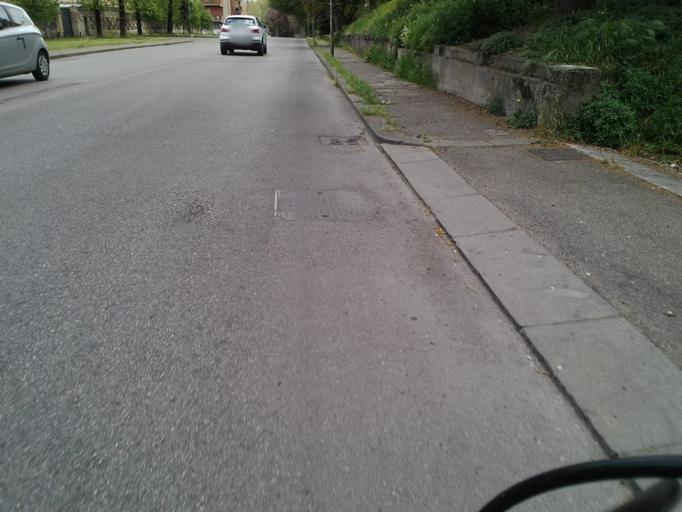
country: IT
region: Veneto
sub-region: Provincia di Verona
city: Verona
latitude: 45.4389
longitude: 10.9780
